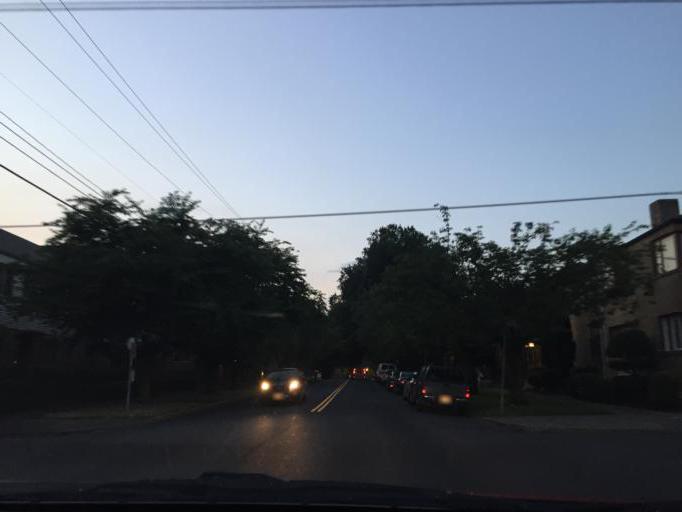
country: US
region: Oregon
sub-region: Multnomah County
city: Portland
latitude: 45.5329
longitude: -122.6448
